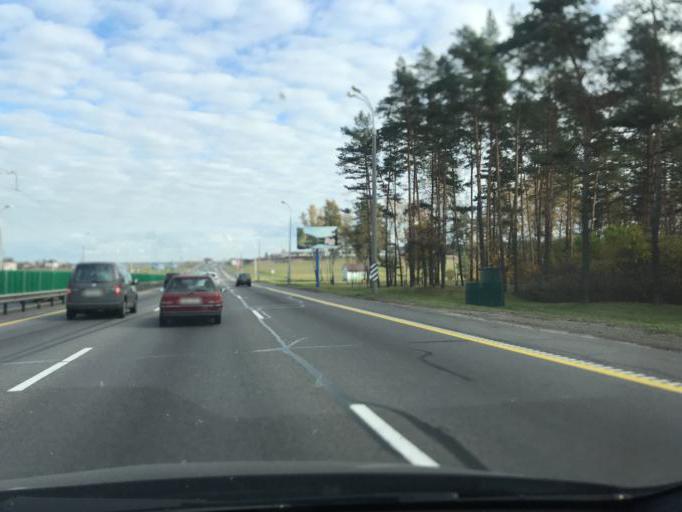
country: BY
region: Minsk
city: Syomkava
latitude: 53.9676
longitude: 27.4912
